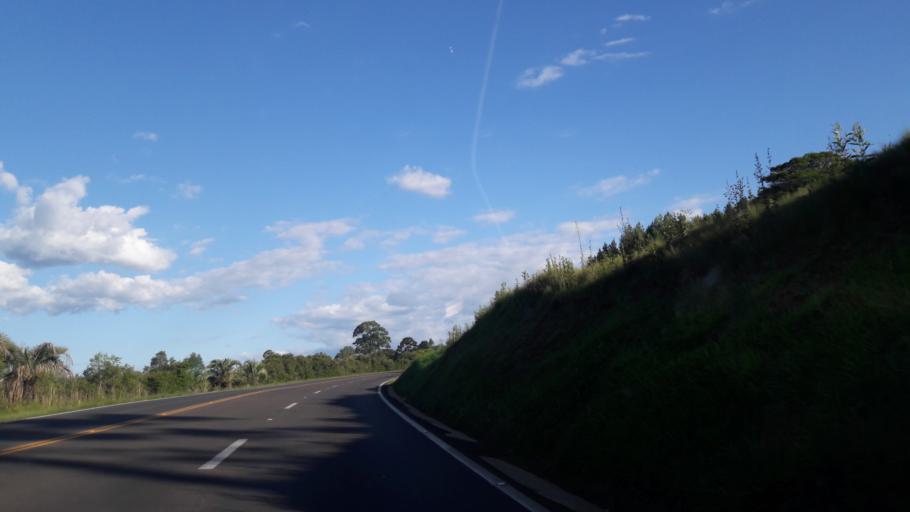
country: BR
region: Parana
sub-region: Guarapuava
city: Guarapuava
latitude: -25.3600
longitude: -51.3532
